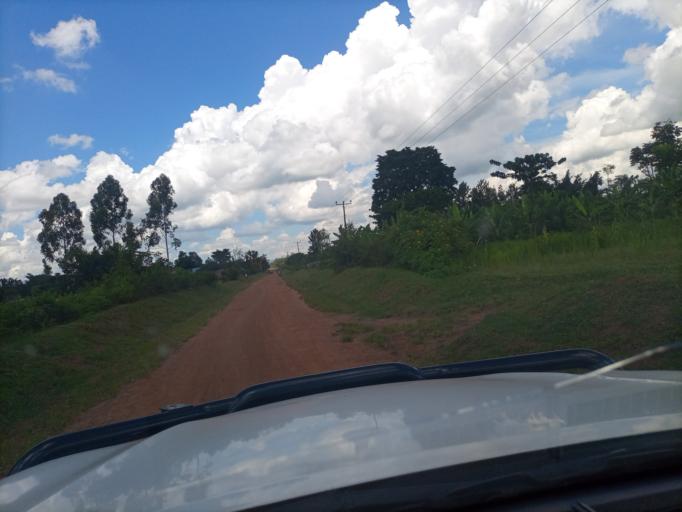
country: UG
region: Eastern Region
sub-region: Tororo District
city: Tororo
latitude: 0.6743
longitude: 34.0051
